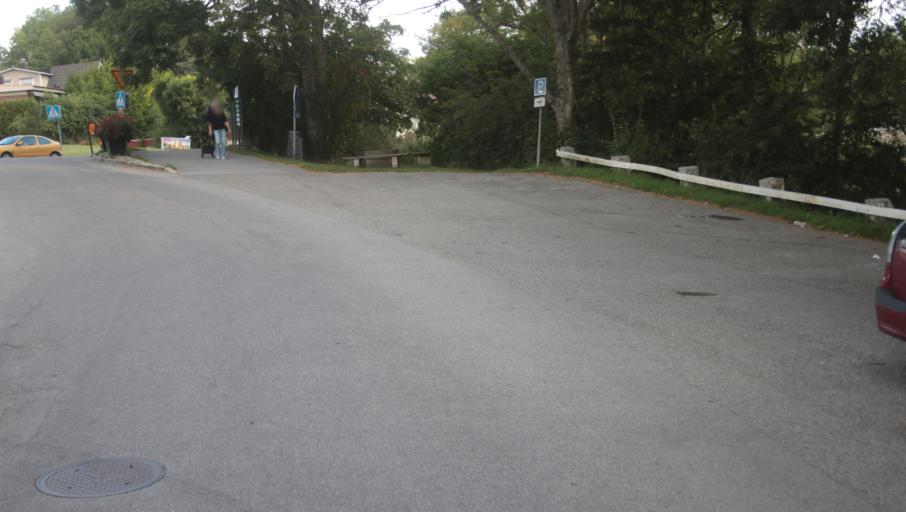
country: SE
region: Blekinge
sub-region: Karlshamns Kommun
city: Morrum
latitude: 56.1925
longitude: 14.7475
